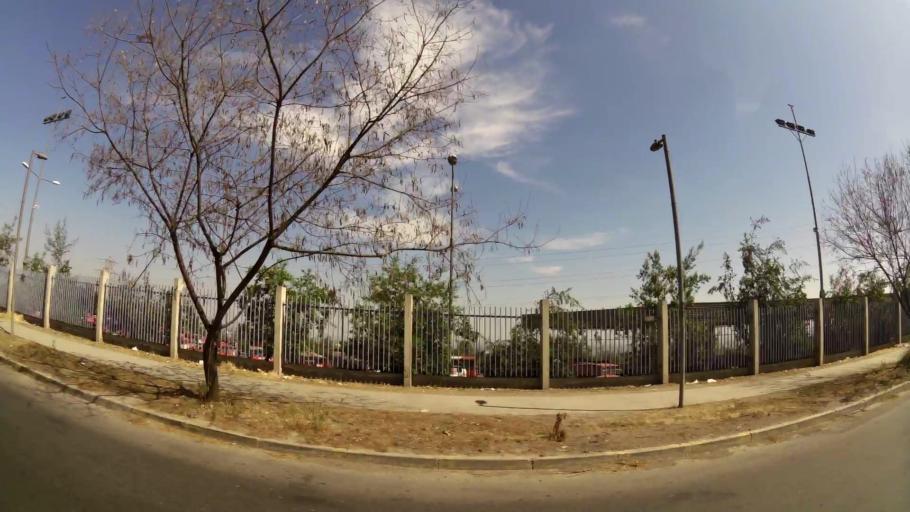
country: CL
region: Santiago Metropolitan
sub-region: Provincia de Santiago
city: Villa Presidente Frei, Nunoa, Santiago, Chile
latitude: -33.4636
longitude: -70.5307
